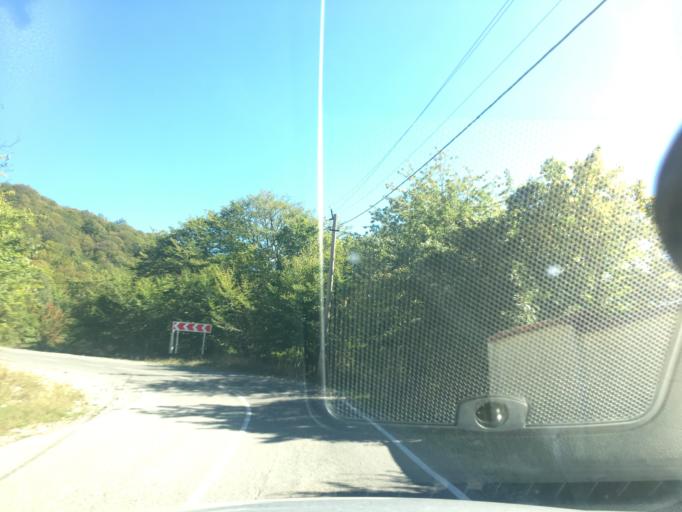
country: GE
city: Didi Lilo
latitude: 41.8871
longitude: 44.9218
